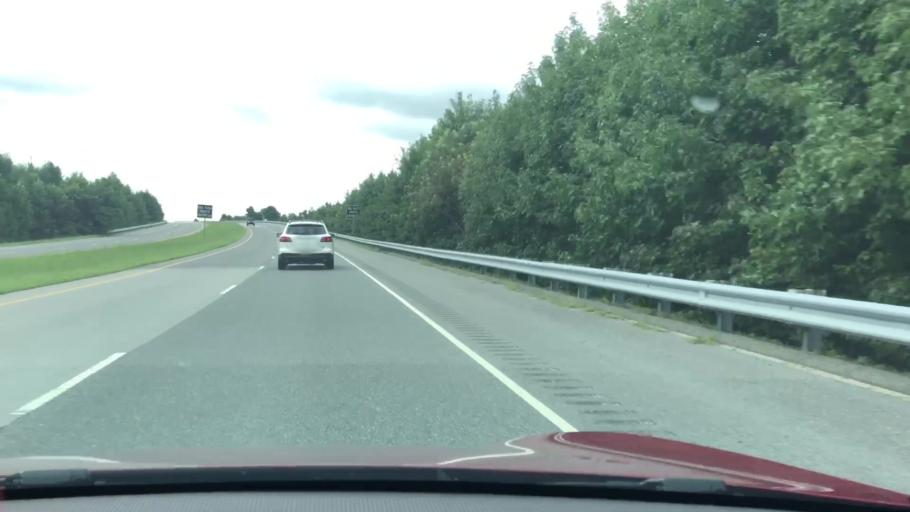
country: US
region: North Carolina
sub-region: Currituck County
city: Moyock
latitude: 36.6213
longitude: -76.2129
